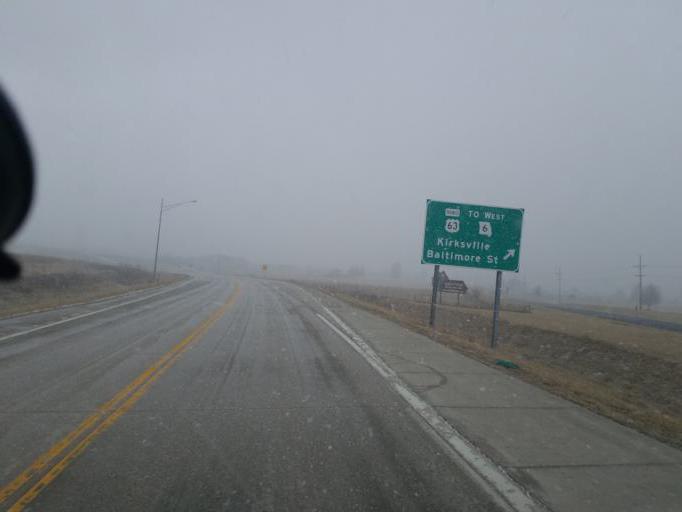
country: US
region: Missouri
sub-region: Adair County
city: Kirksville
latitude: 40.2434
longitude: -92.5822
